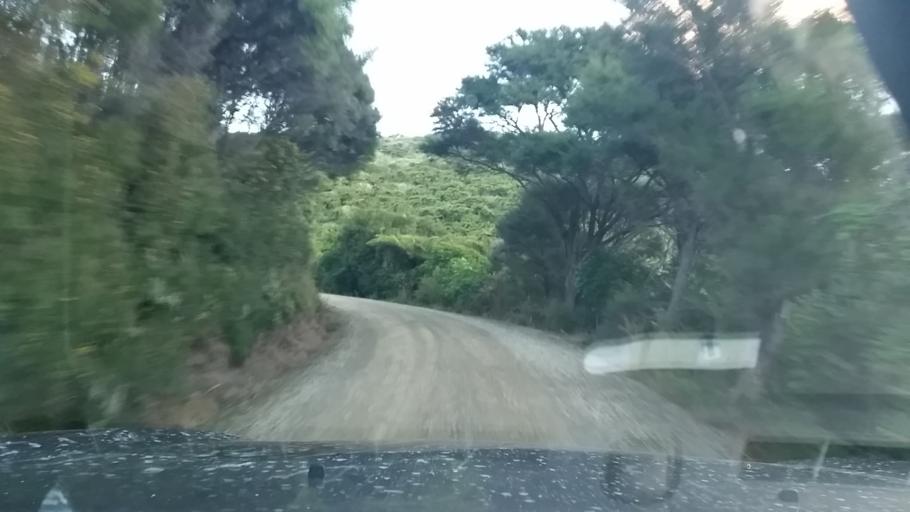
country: NZ
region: Marlborough
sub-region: Marlborough District
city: Picton
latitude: -41.1304
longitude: 174.1503
